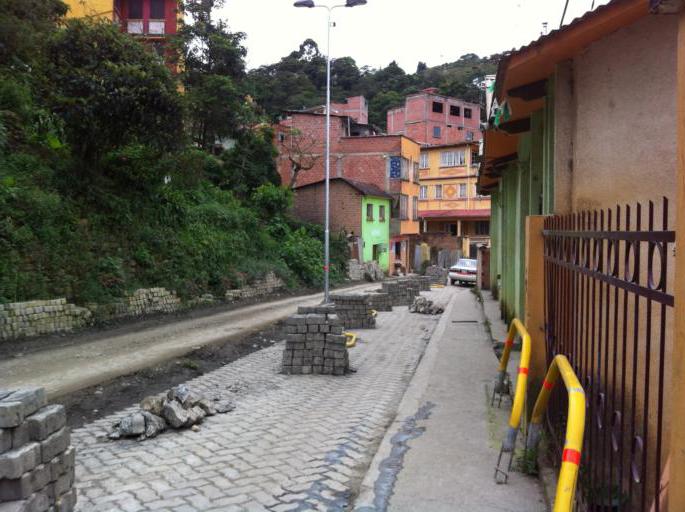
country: BO
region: La Paz
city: Coroico
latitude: -16.1901
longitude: -67.7270
